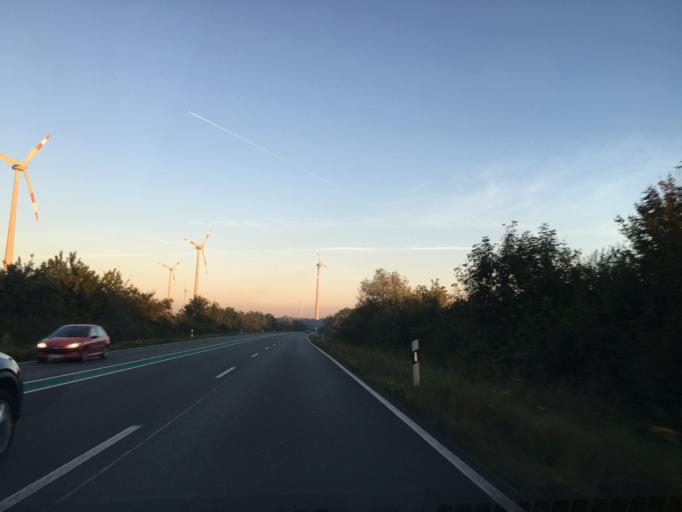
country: DE
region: North Rhine-Westphalia
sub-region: Regierungsbezirk Munster
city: Altenberge
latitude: 52.0753
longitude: 7.4269
